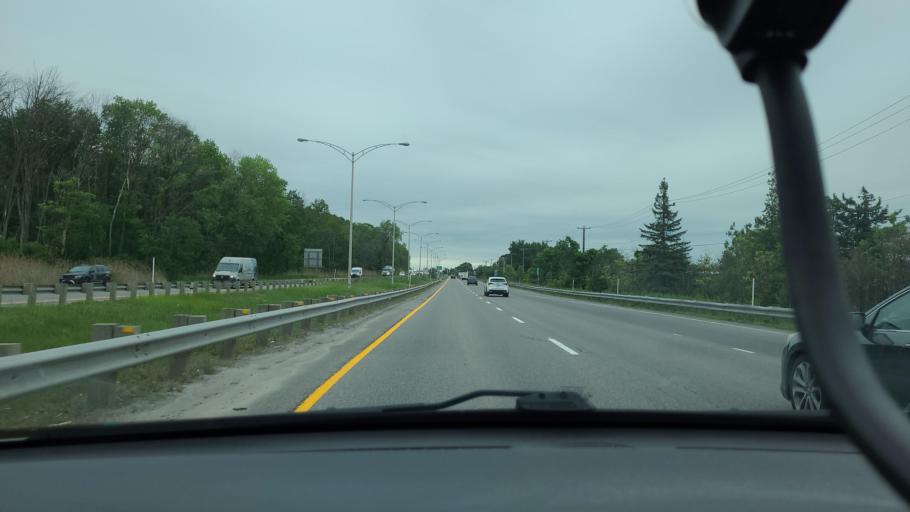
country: CA
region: Quebec
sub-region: Lanaudiere
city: Terrebonne
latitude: 45.7087
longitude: -73.6439
